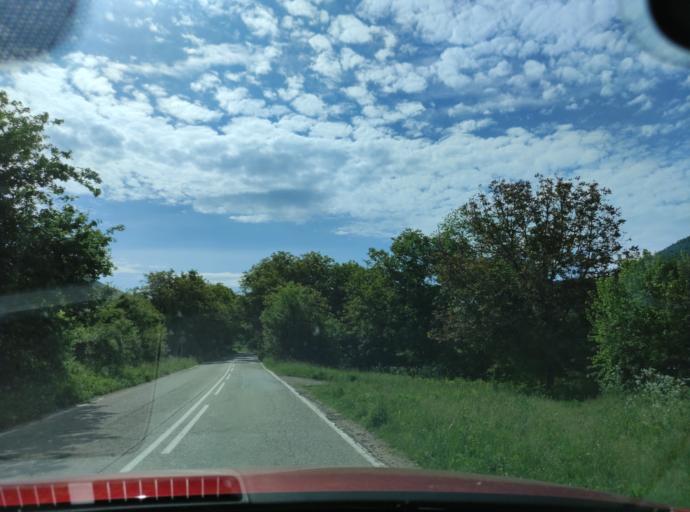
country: BG
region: Montana
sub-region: Obshtina Chiprovtsi
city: Chiprovtsi
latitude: 43.4888
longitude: 22.8117
